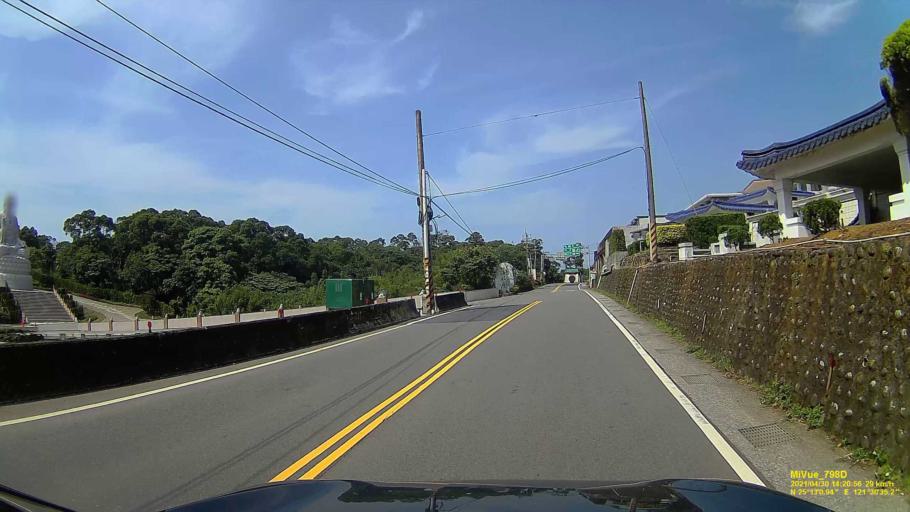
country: TW
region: Taipei
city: Taipei
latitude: 25.2170
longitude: 121.5098
